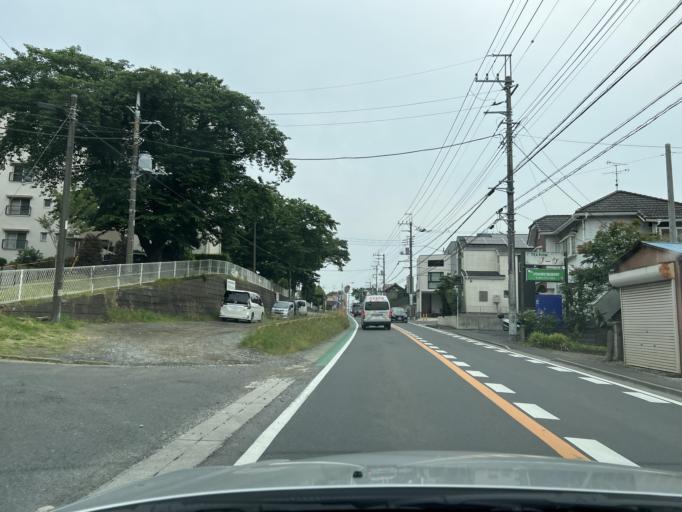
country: JP
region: Chiba
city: Matsudo
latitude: 35.7563
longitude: 139.9400
